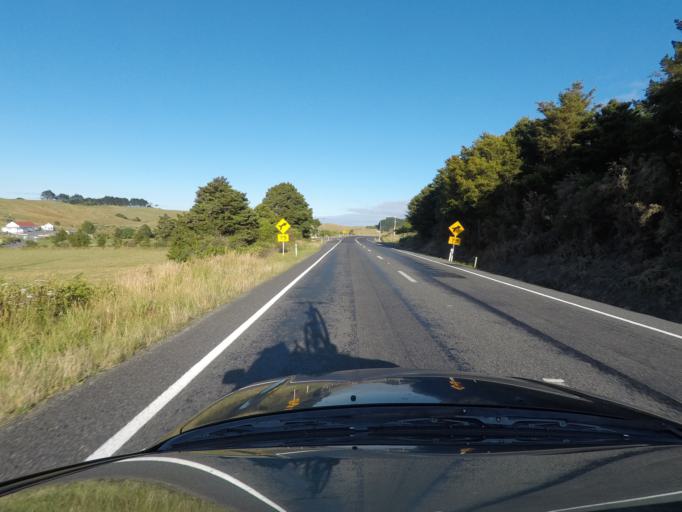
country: NZ
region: Northland
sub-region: Far North District
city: Kawakawa
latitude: -35.4932
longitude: 174.1356
